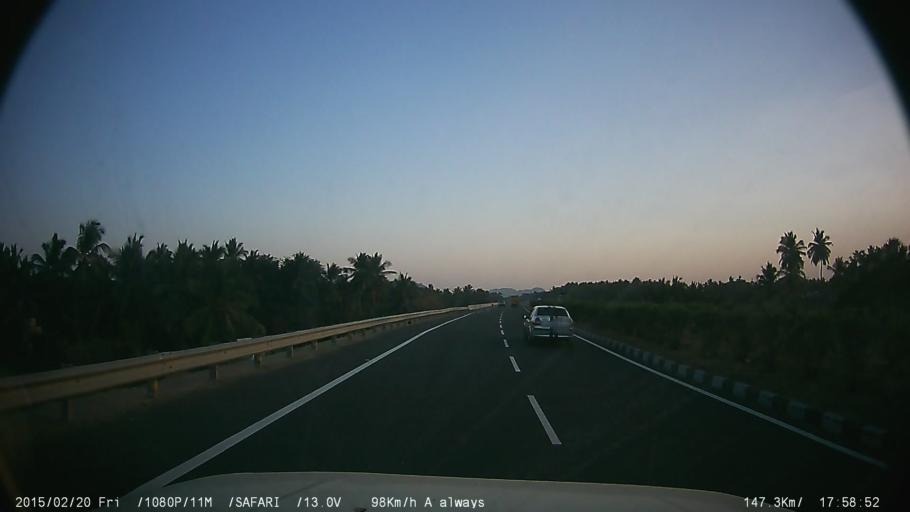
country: IN
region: Tamil Nadu
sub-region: Krishnagiri
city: Kaverippattanam
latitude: 12.4246
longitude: 78.2268
